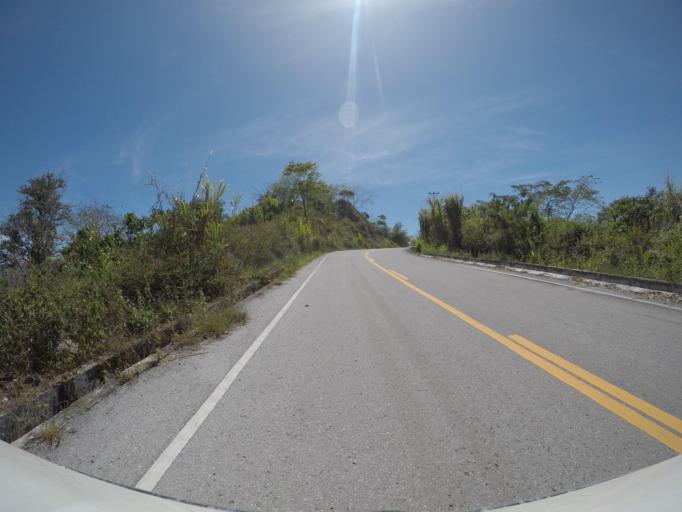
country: TL
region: Manatuto
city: Manatuto
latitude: -8.8700
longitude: 125.9951
